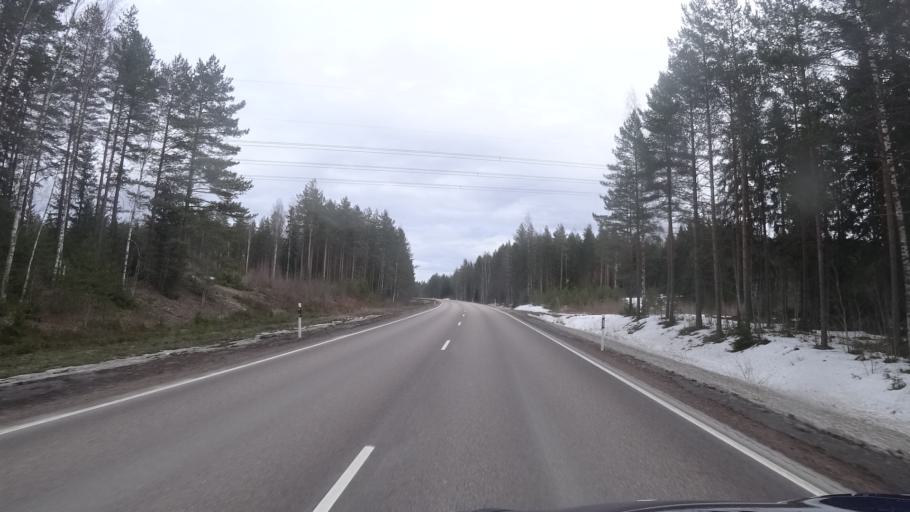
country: FI
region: Kymenlaakso
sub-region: Kouvola
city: Anjala
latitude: 60.6929
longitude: 26.6705
